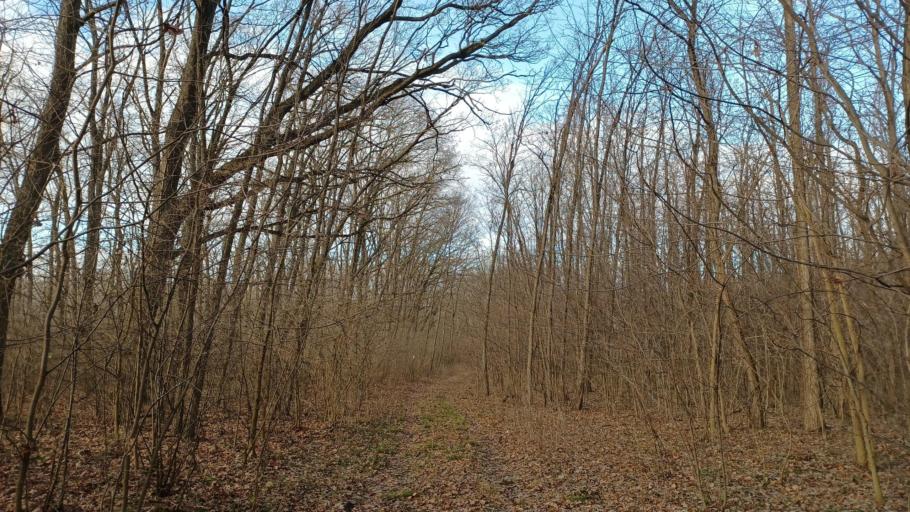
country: HU
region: Tolna
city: Tengelic
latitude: 46.5436
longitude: 18.6933
